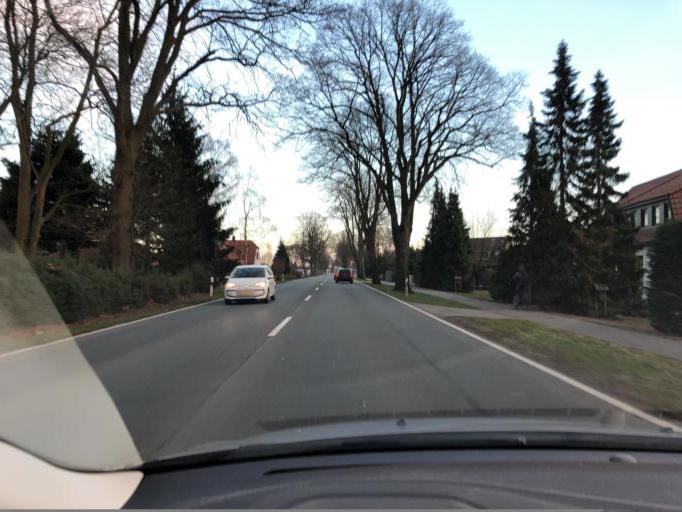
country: DE
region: Lower Saxony
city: Stuhr
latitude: 52.9914
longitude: 8.7729
